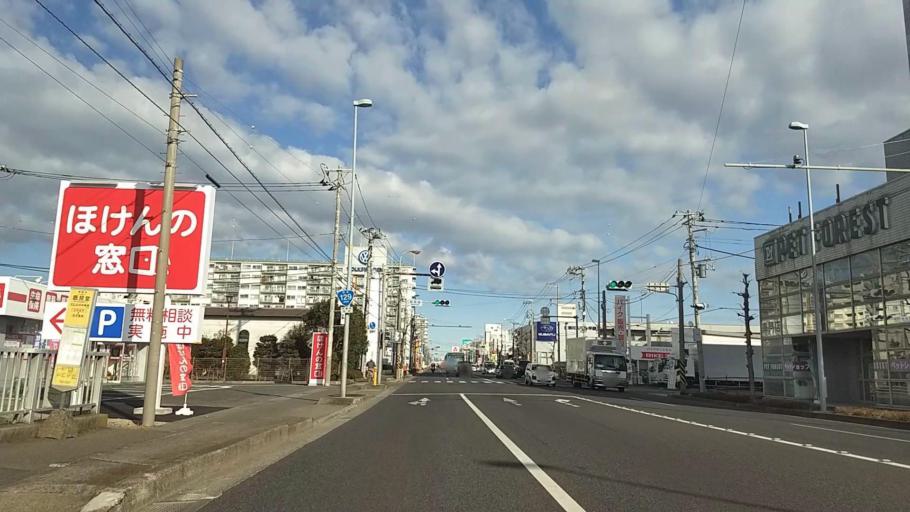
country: JP
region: Kanagawa
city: Hiratsuka
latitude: 35.3675
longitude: 139.3615
